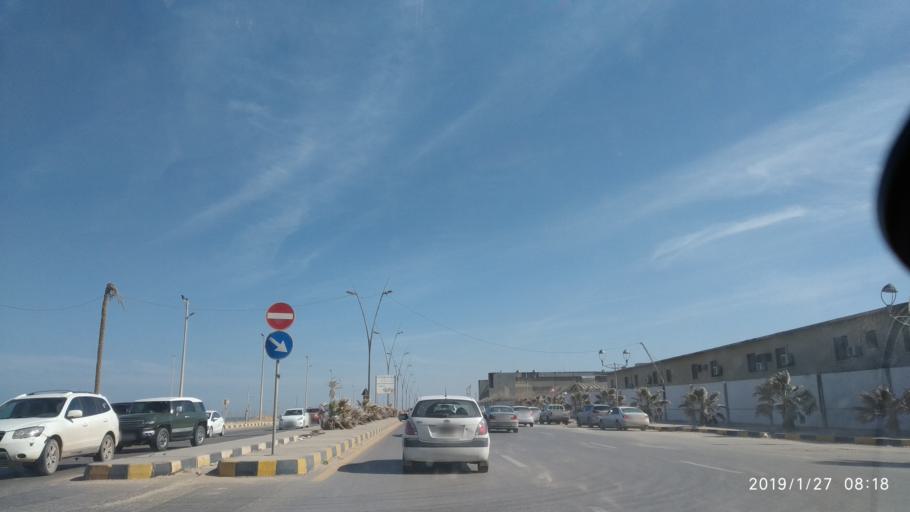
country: LY
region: Tripoli
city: Tagiura
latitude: 32.9078
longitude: 13.2717
